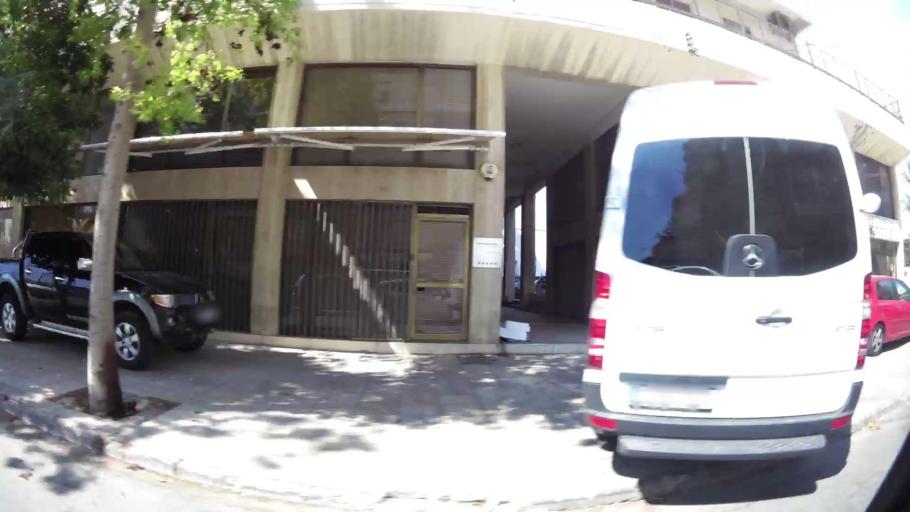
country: CY
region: Larnaka
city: Larnaca
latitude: 34.9159
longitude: 33.6283
